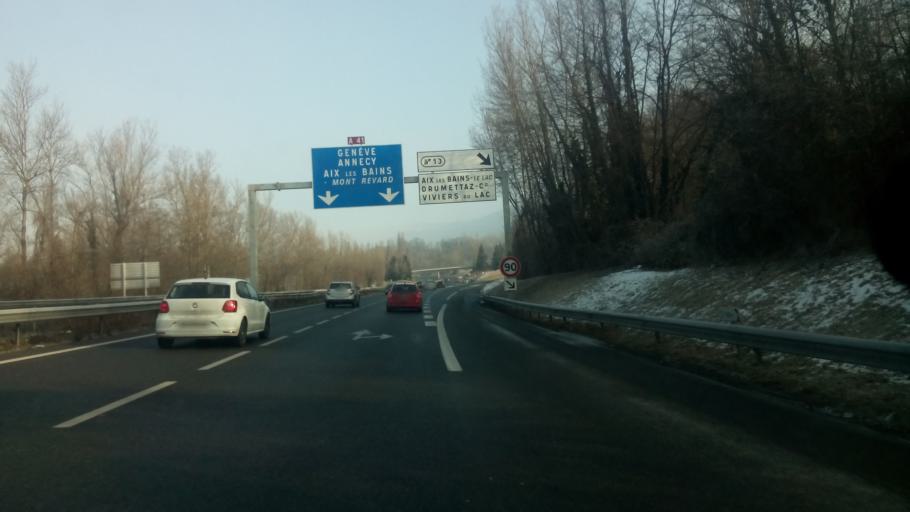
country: FR
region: Rhone-Alpes
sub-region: Departement de la Savoie
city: Drumettaz-Clarafond
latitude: 45.6488
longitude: 5.9221
